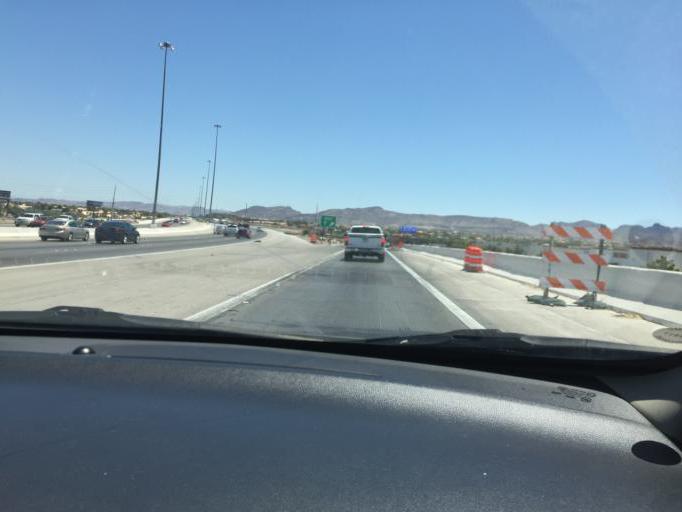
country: US
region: Nevada
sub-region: Clark County
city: Whitney
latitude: 36.0239
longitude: -115.1236
